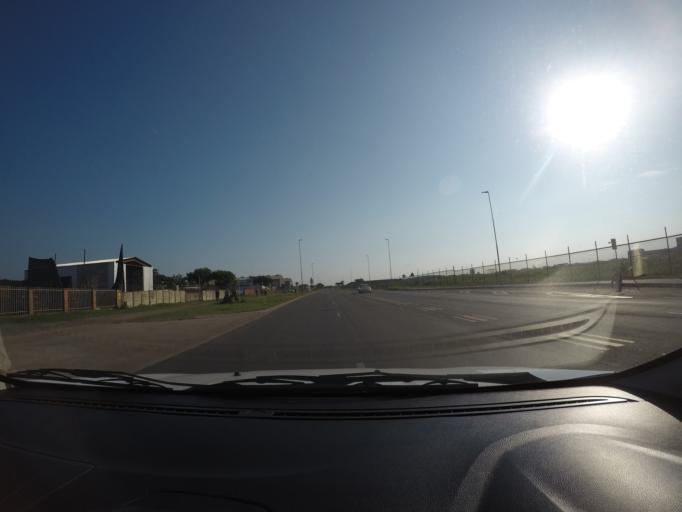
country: ZA
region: KwaZulu-Natal
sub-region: uThungulu District Municipality
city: Richards Bay
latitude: -28.7442
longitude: 32.0342
